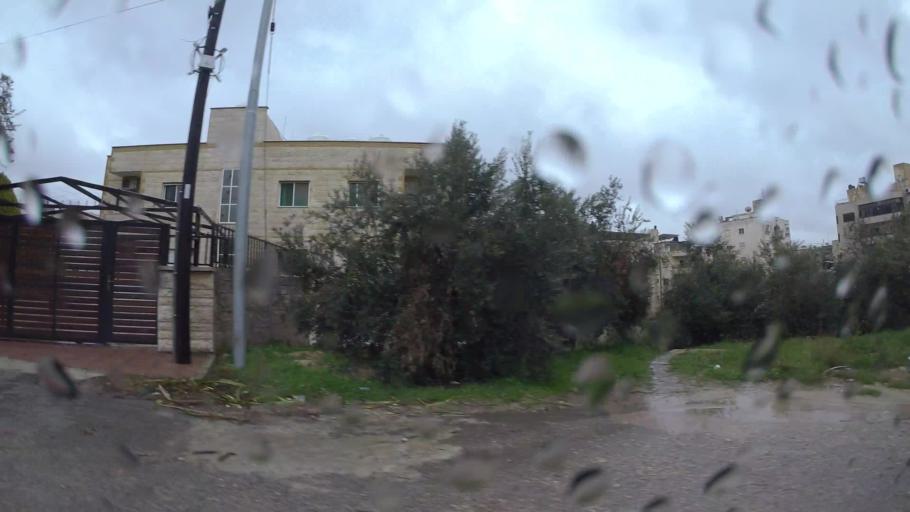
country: JO
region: Amman
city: Al Jubayhah
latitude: 32.0213
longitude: 35.8678
